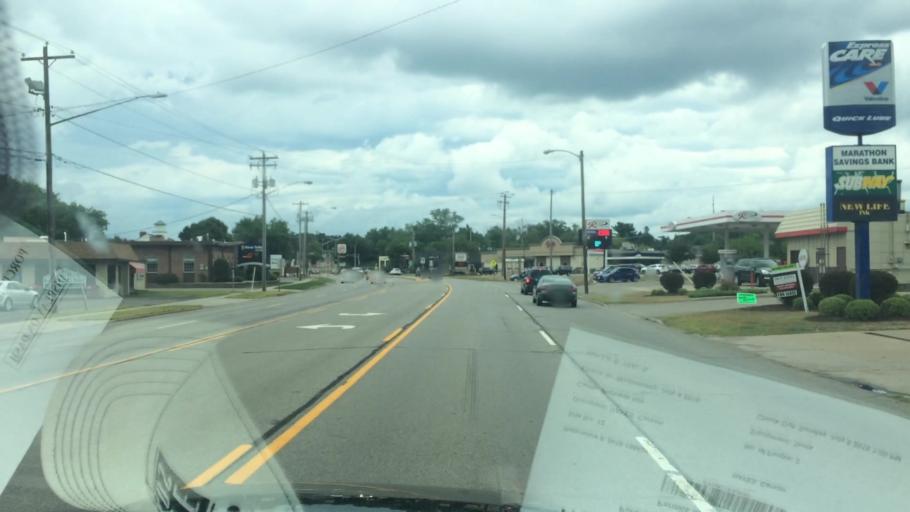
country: US
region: Wisconsin
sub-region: Marathon County
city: Schofield
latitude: 44.8998
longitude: -89.6099
